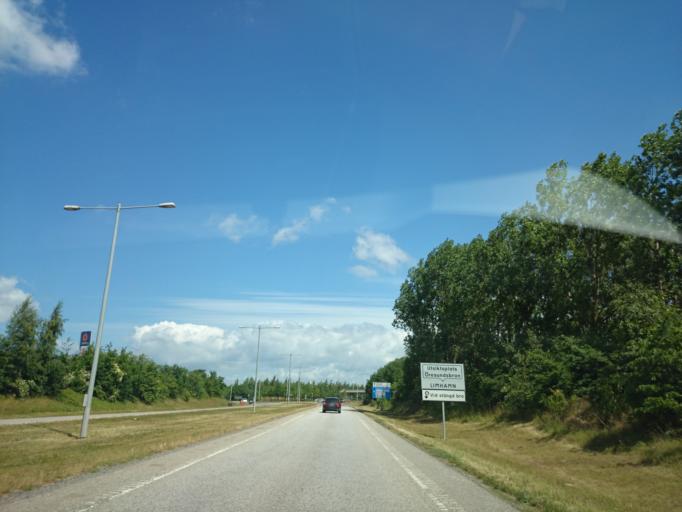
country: SE
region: Skane
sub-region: Malmo
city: Bunkeflostrand
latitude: 55.5542
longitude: 12.9542
